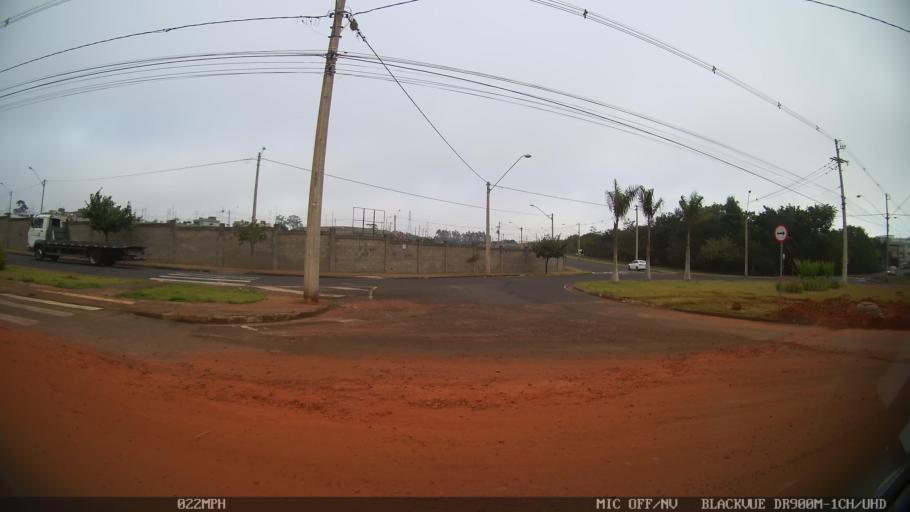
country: BR
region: Sao Paulo
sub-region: Sao Jose Do Rio Preto
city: Sao Jose do Rio Preto
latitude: -20.8495
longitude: -49.3701
